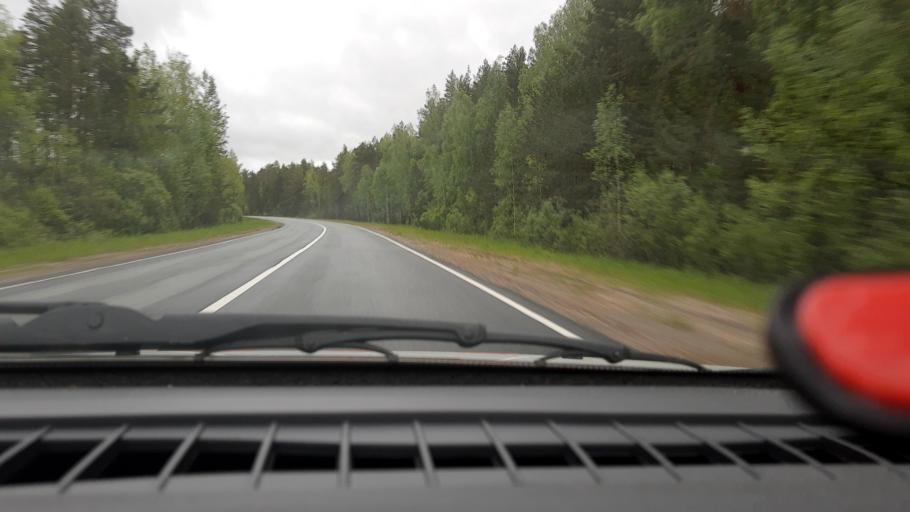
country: RU
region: Nizjnij Novgorod
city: Krasnyye Baki
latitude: 57.1735
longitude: 45.3238
